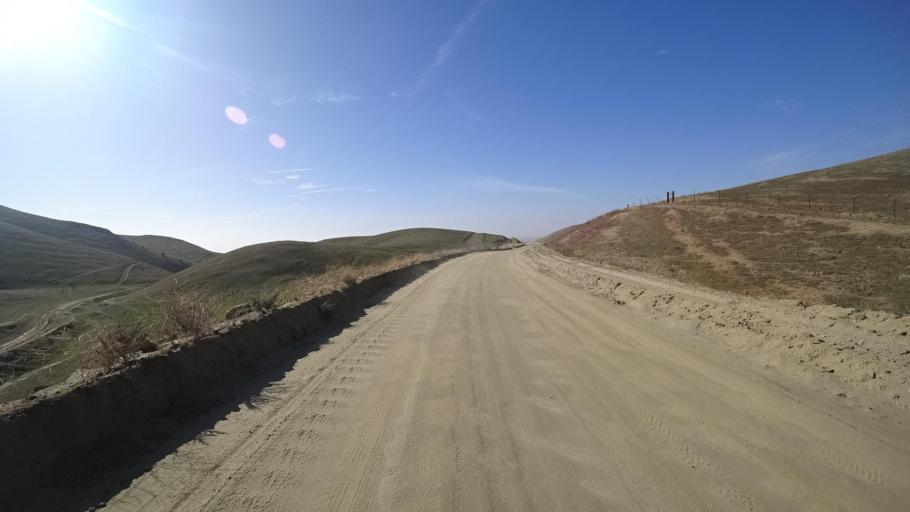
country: US
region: California
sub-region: Kern County
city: Oildale
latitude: 35.4847
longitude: -118.8161
